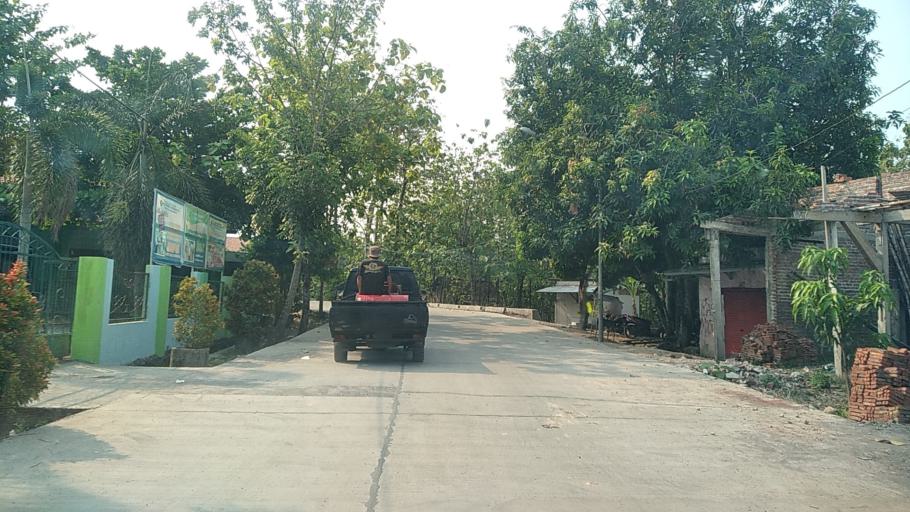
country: ID
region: Central Java
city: Mranggen
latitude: -7.0710
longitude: 110.4696
